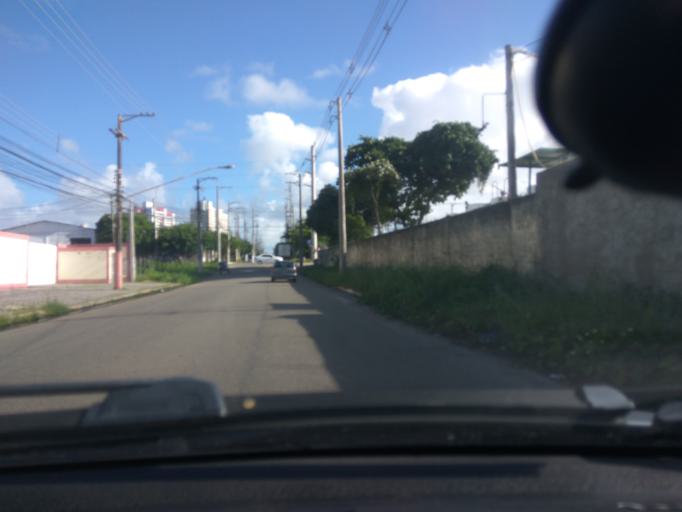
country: BR
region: Sergipe
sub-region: Aracaju
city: Aracaju
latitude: -10.9479
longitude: -37.0668
